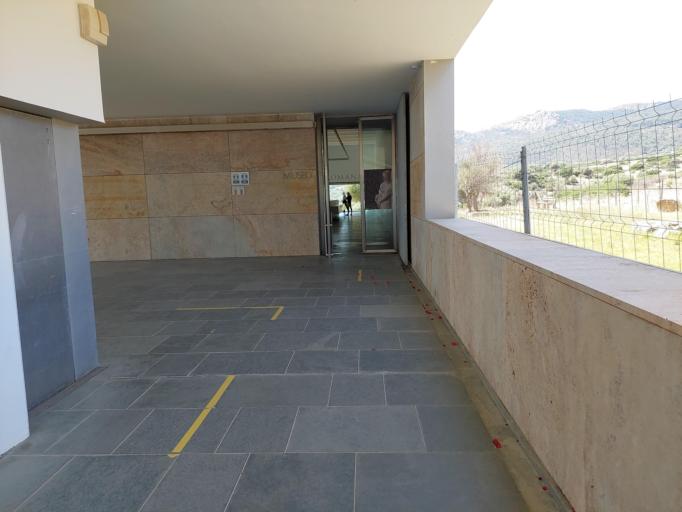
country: ES
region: Andalusia
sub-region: Provincia de Cadiz
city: Zahara de los Atunes
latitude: 36.0901
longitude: -5.7719
